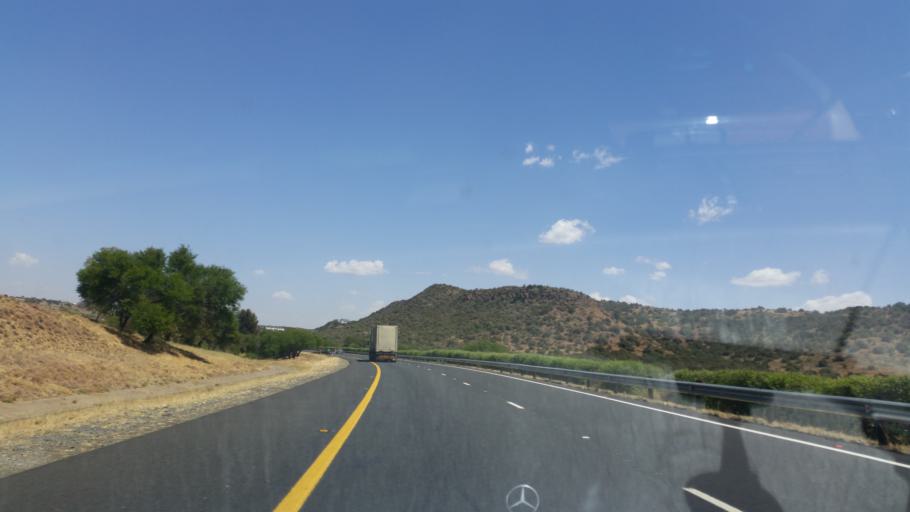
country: ZA
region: Orange Free State
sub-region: Mangaung Metropolitan Municipality
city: Bloemfontein
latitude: -28.9806
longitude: 26.2824
